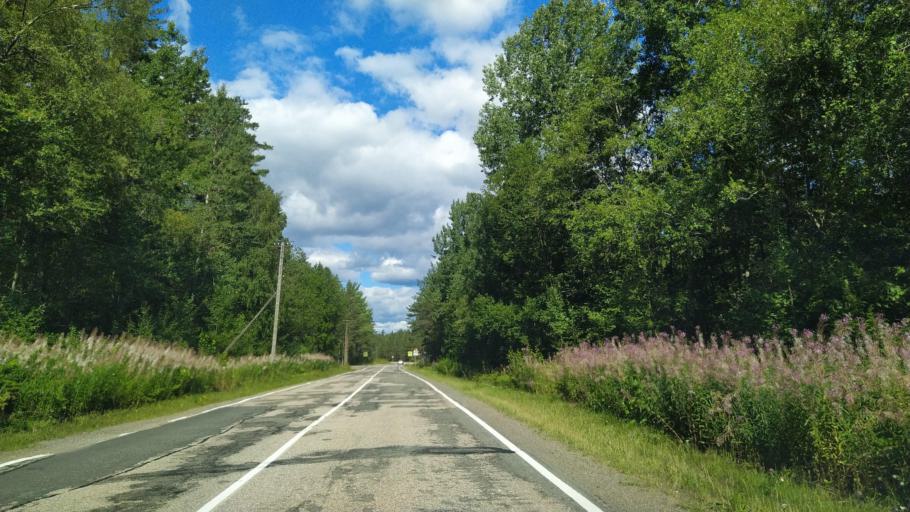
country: RU
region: Leningrad
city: Priozersk
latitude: 60.9747
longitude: 30.2806
